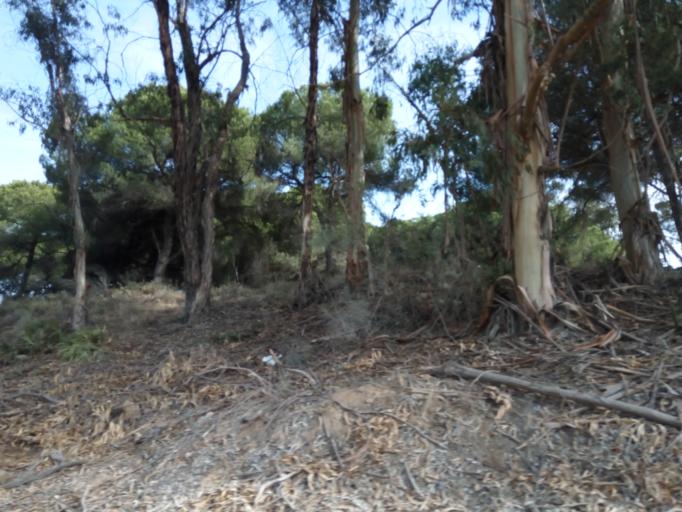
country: PT
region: Faro
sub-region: Faro
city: Faro
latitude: 37.0345
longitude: -7.9800
